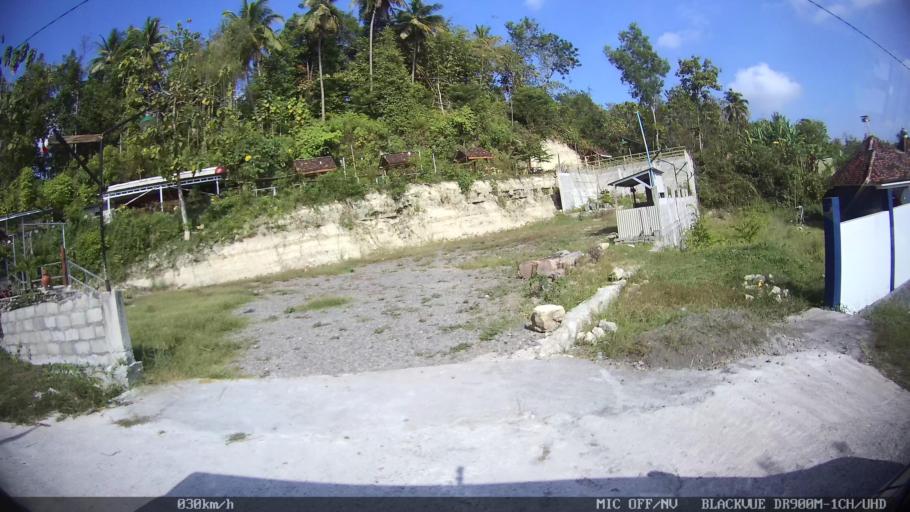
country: ID
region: Daerah Istimewa Yogyakarta
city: Kasihan
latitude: -7.8146
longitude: 110.2988
